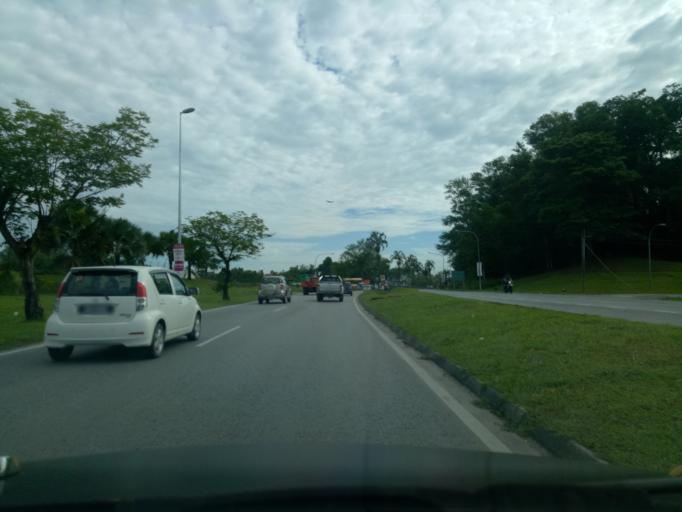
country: MY
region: Sarawak
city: Kuching
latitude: 1.4563
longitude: 110.3250
